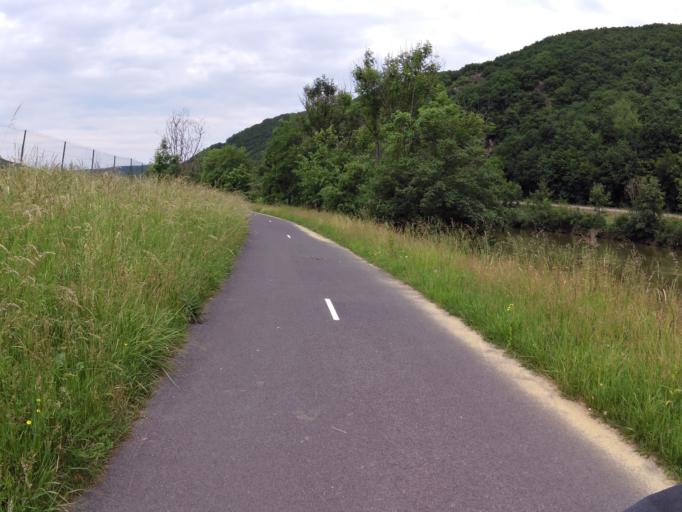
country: FR
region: Champagne-Ardenne
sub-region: Departement des Ardennes
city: Nouzonville
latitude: 49.7990
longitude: 4.7572
